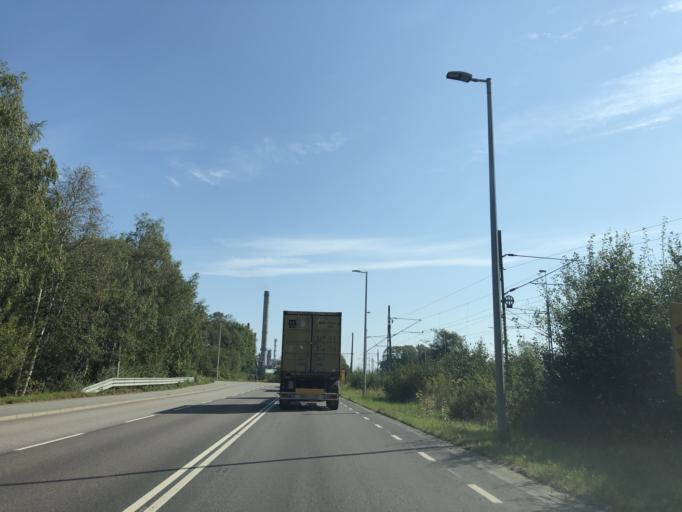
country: SE
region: Vaestra Goetaland
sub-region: Goteborg
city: Majorna
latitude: 57.6999
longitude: 11.8672
